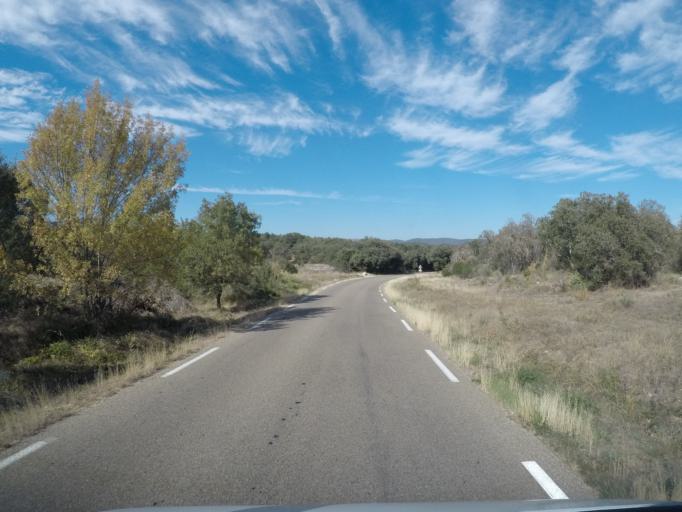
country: FR
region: Languedoc-Roussillon
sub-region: Departement du Gard
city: Boisset-et-Gaujac
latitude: 44.0133
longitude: 3.9936
